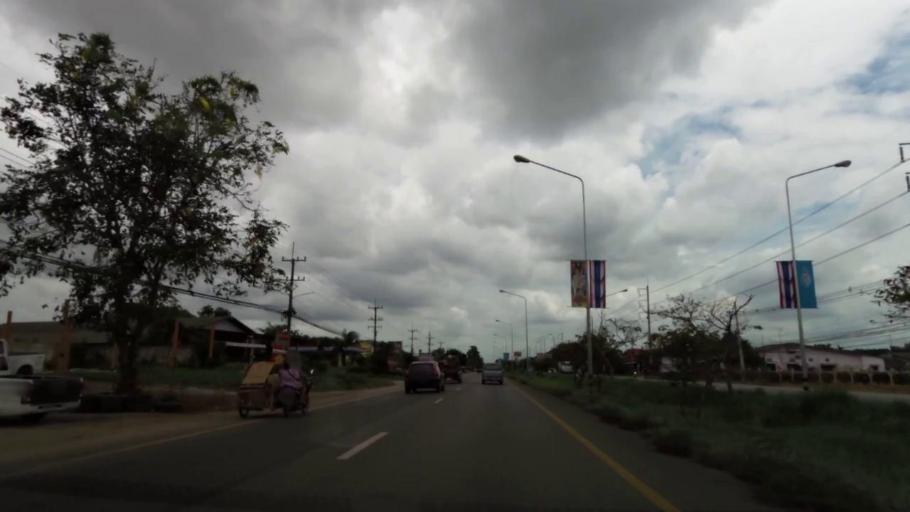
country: TH
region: Rayong
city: Klaeng
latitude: 12.7801
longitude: 101.6996
